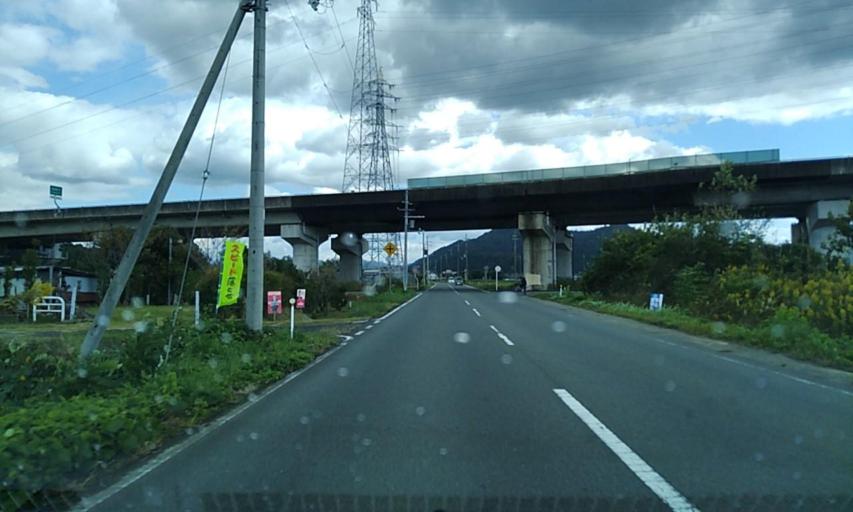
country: JP
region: Kyoto
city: Ayabe
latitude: 35.3069
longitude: 135.1912
